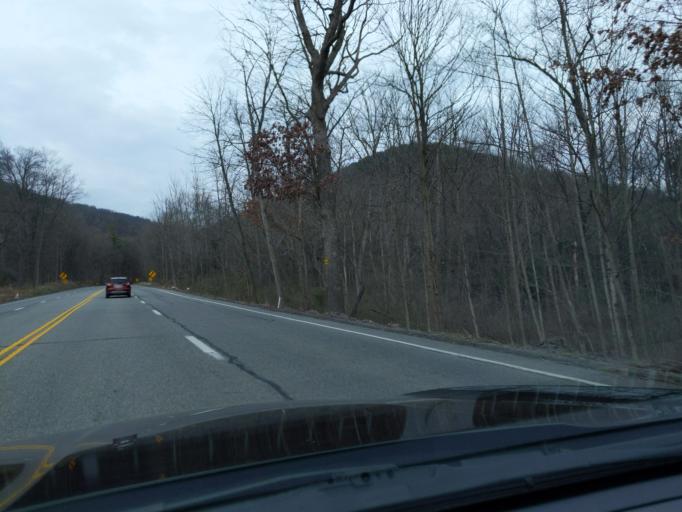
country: US
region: Pennsylvania
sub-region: Blair County
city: Williamsburg
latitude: 40.4920
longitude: -78.2451
